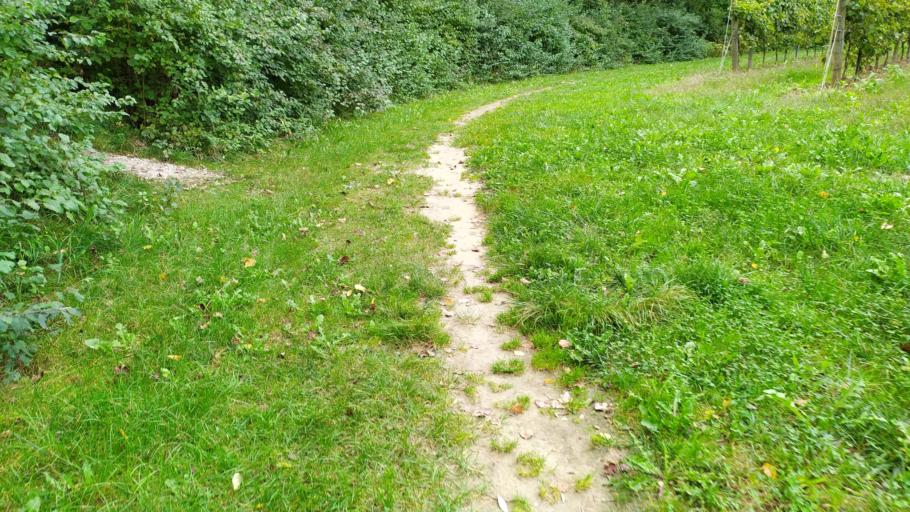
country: IT
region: Veneto
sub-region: Provincia di Treviso
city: Conegliano
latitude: 45.9017
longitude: 12.2949
